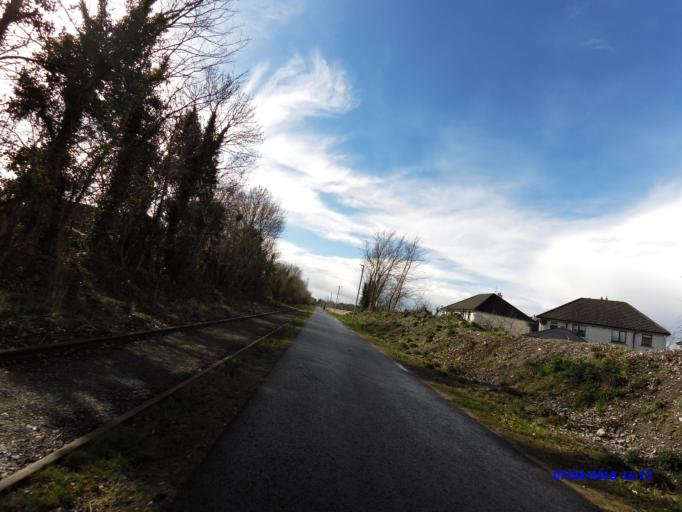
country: IE
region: Leinster
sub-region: An Iarmhi
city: Athlone
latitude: 53.4252
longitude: -7.9157
